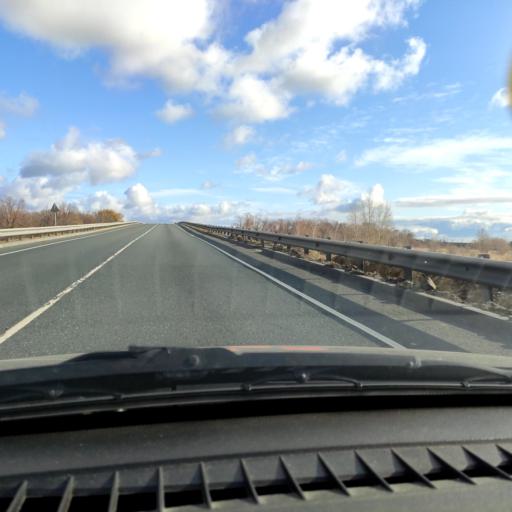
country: RU
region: Samara
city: Balasheyka
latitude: 53.1892
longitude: 48.2101
